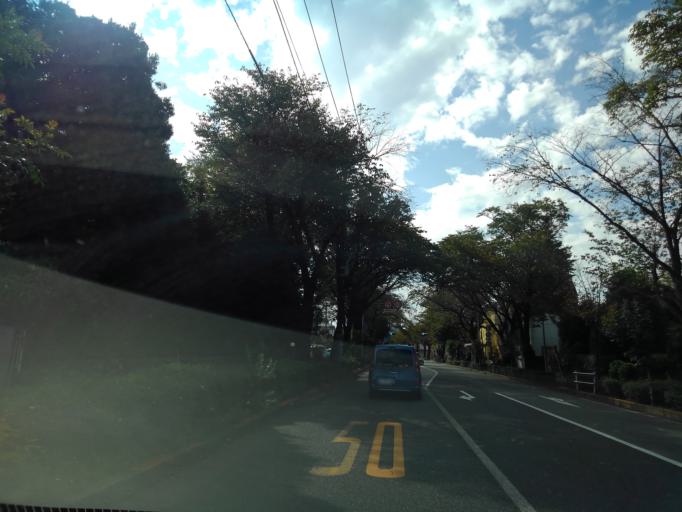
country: JP
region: Tokyo
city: Kokubunji
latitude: 35.6917
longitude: 139.4981
